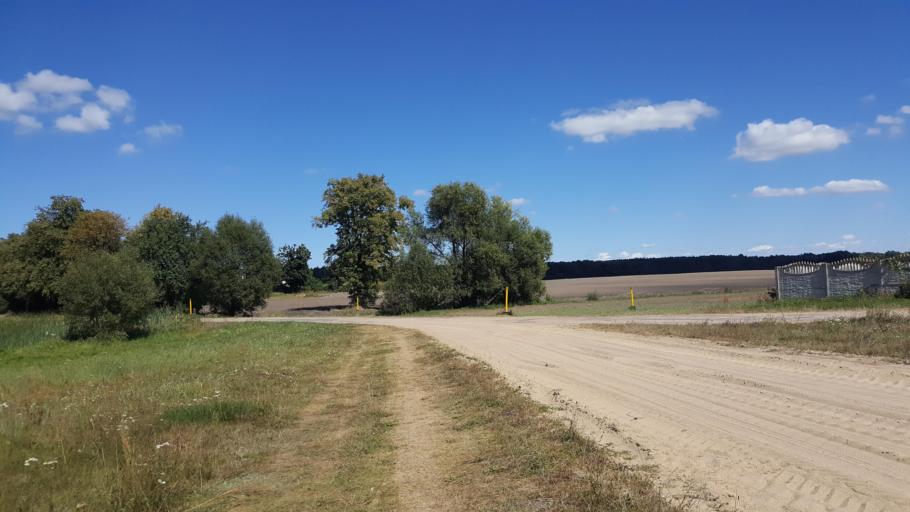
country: BY
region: Brest
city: Vysokaye
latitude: 52.2580
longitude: 23.4287
